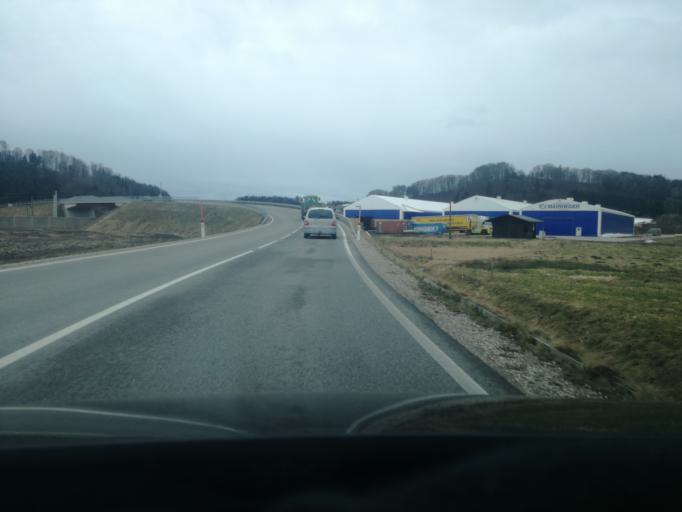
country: AT
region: Upper Austria
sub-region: Politischer Bezirk Vocklabruck
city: Neukirchen an der Vockla
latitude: 48.0286
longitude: 13.5089
